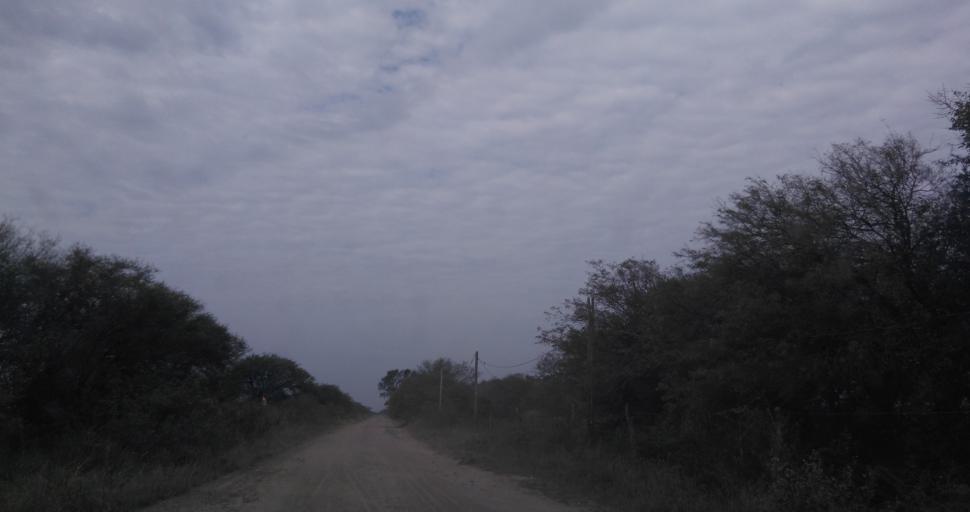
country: AR
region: Chaco
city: Fontana
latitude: -27.4583
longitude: -59.0503
